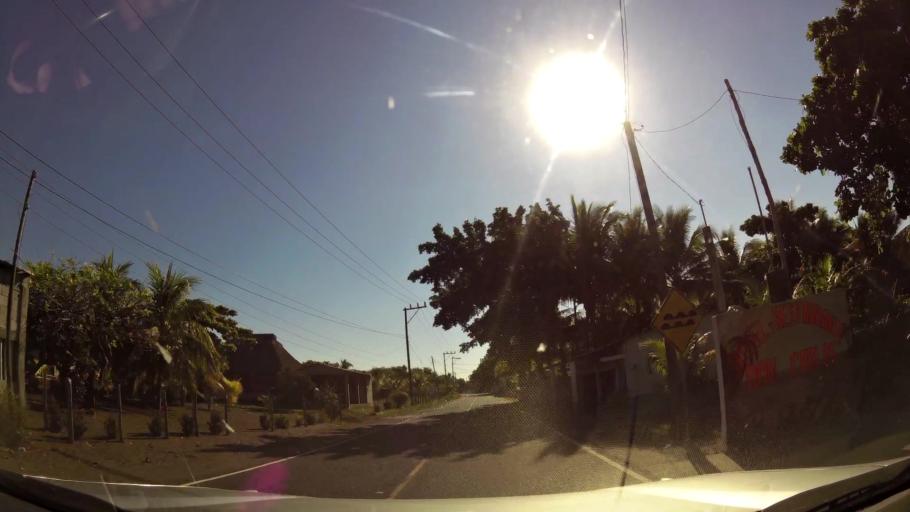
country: GT
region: Santa Rosa
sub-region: Municipio de Taxisco
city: Taxisco
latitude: 13.8844
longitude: -90.4602
